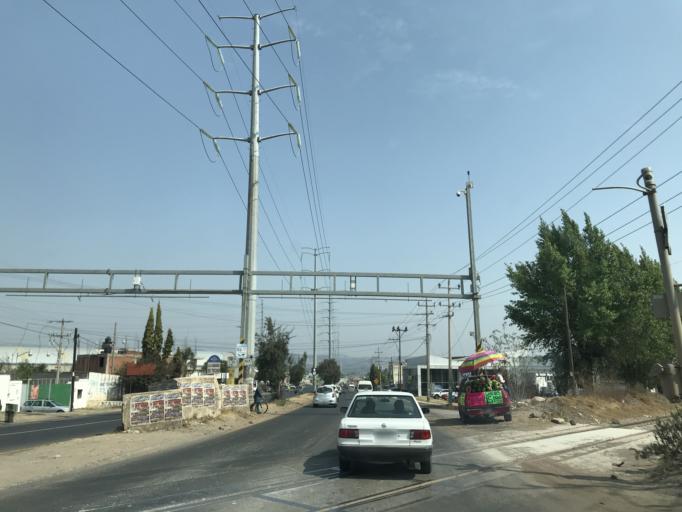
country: MX
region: Tlaxcala
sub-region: Chiautempan
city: Santa Cruz Tetela
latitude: 19.2981
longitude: -98.1955
